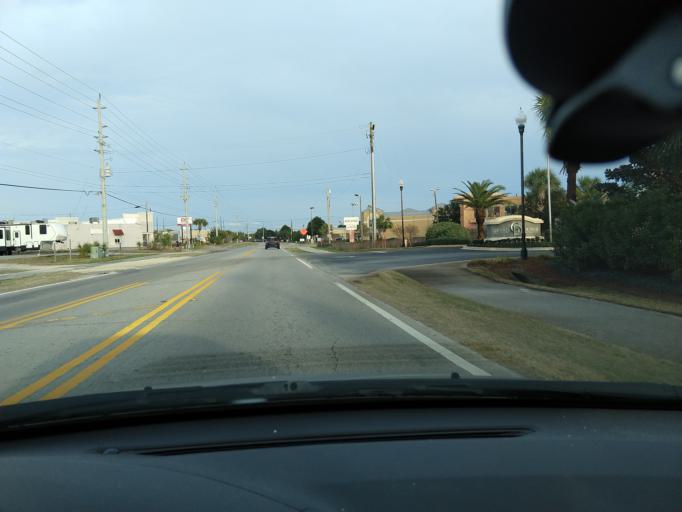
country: US
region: Florida
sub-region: Walton County
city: Miramar Beach
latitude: 30.3759
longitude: -86.3522
